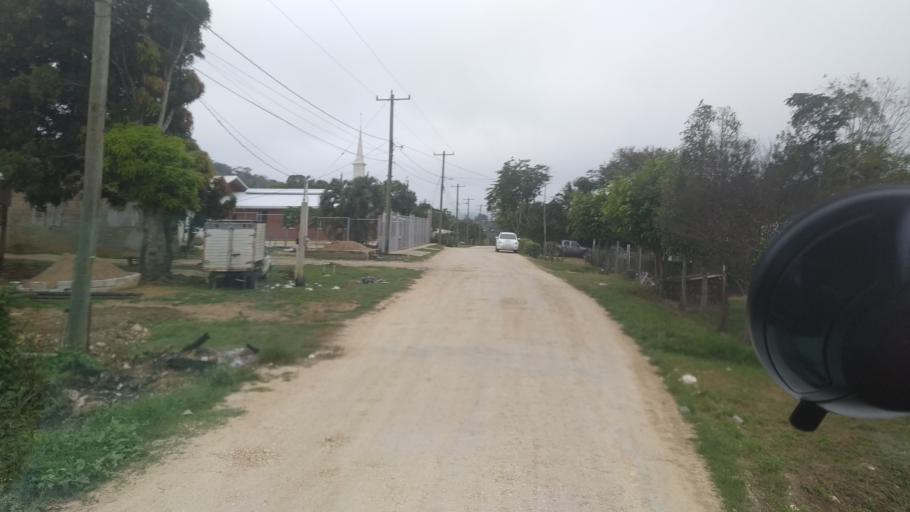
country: BZ
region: Cayo
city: Benque Viejo del Carmen
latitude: 17.0833
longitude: -89.1249
